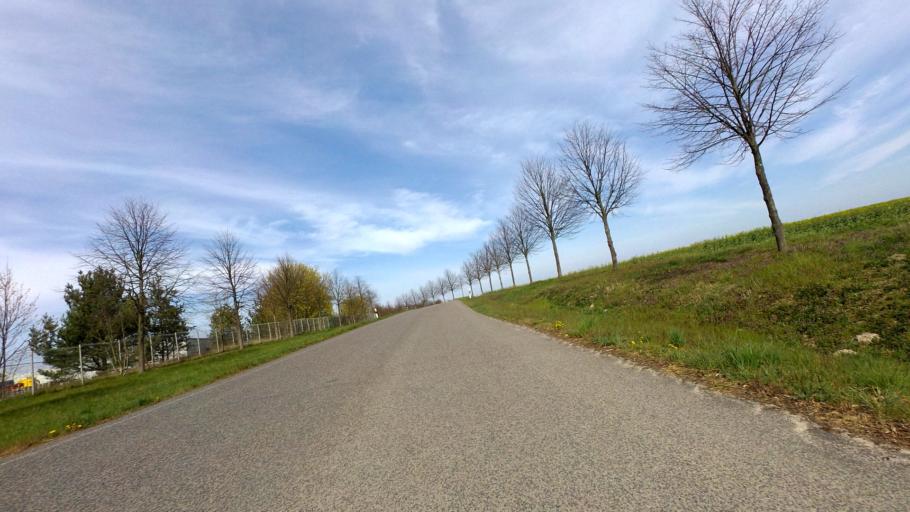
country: DE
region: Brandenburg
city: Grossbeeren
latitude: 52.3857
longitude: 13.3376
